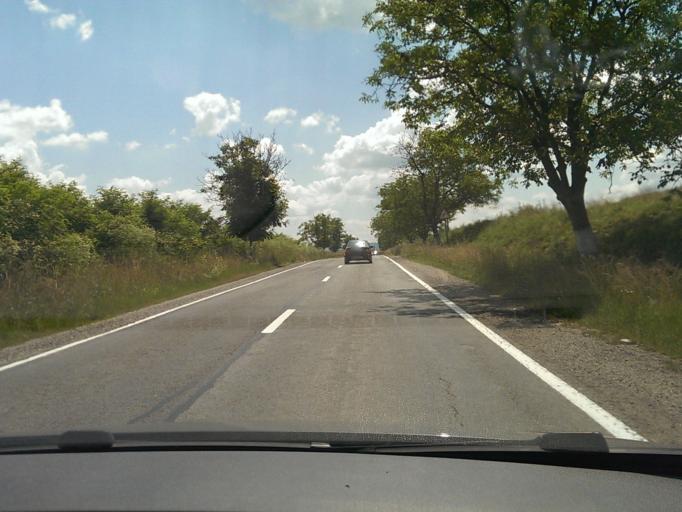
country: RO
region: Cluj
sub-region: Comuna Apahida
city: Apahida
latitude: 46.8052
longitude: 23.7725
